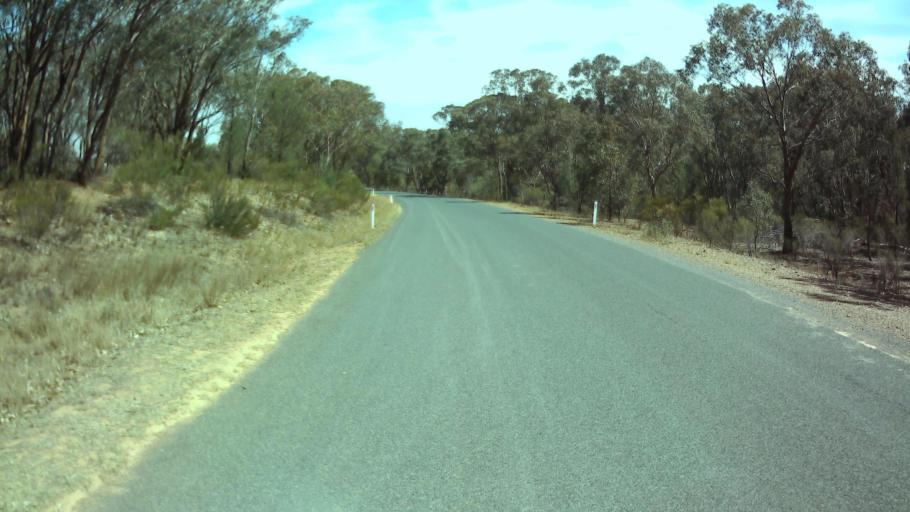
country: AU
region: New South Wales
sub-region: Weddin
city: Grenfell
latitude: -34.0052
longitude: 148.1301
